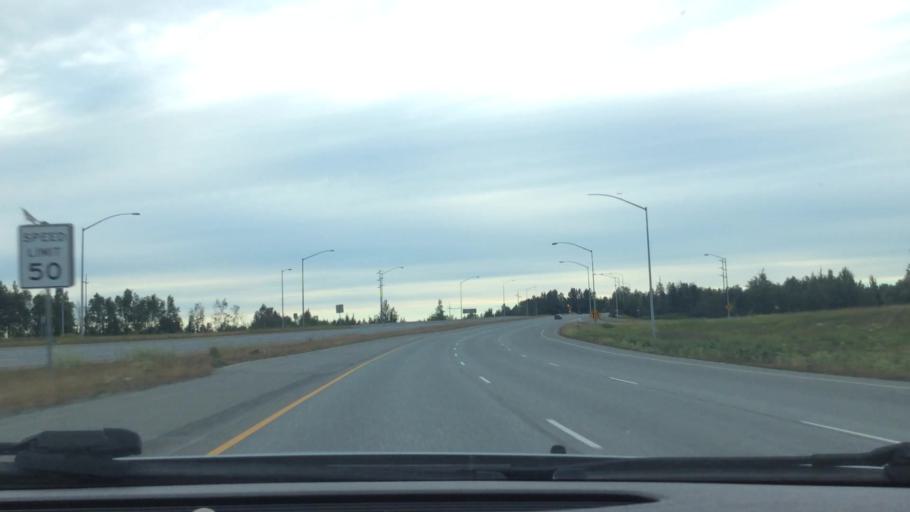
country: US
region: Alaska
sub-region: Anchorage Municipality
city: Anchorage
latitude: 61.1728
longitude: -149.9166
